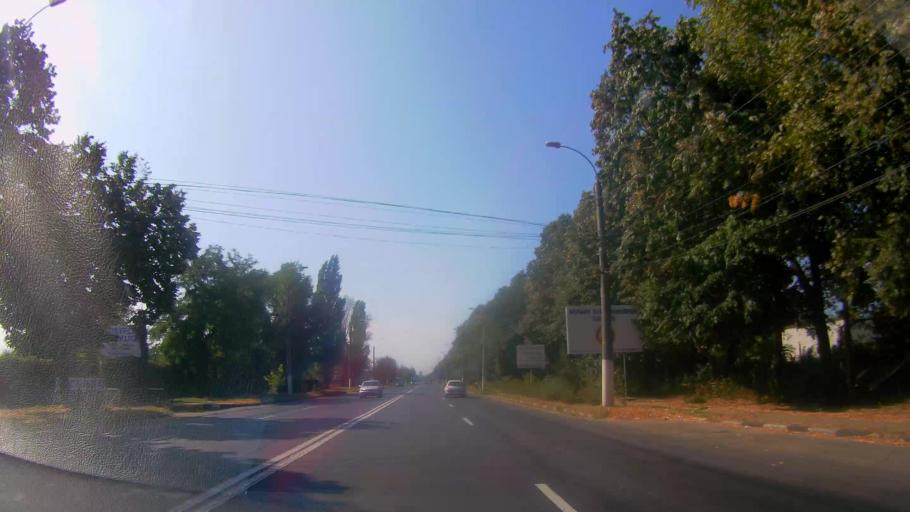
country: RO
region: Giurgiu
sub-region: Comuna Fratesti
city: Remus
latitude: 43.9240
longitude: 25.9741
